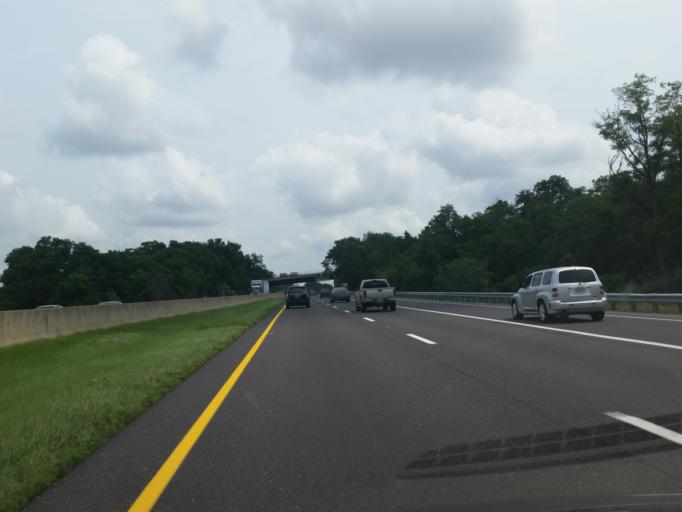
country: US
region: Pennsylvania
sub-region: Dauphin County
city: Progress
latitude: 40.3014
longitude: -76.8284
